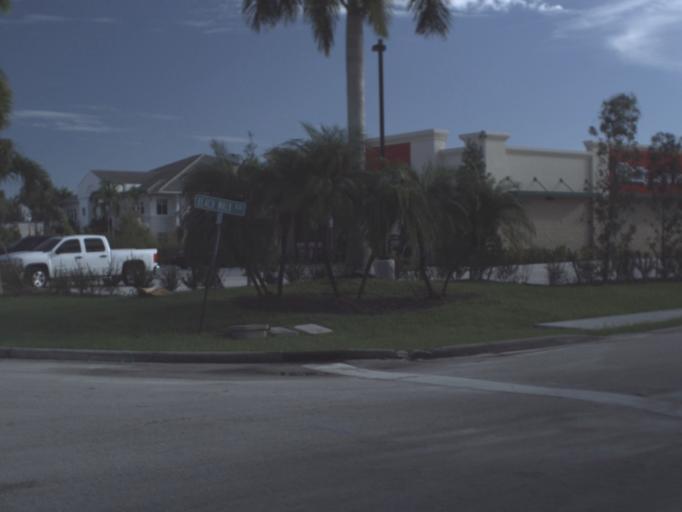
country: US
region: Florida
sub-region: Lee County
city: Harlem Heights
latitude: 26.5122
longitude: -81.9437
